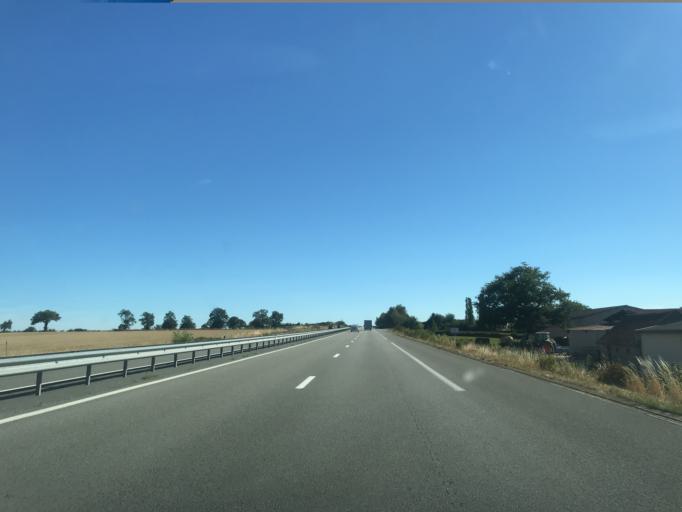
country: FR
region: Limousin
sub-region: Departement de la Creuse
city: Chambon-sur-Voueize
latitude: 46.2753
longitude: 2.3872
